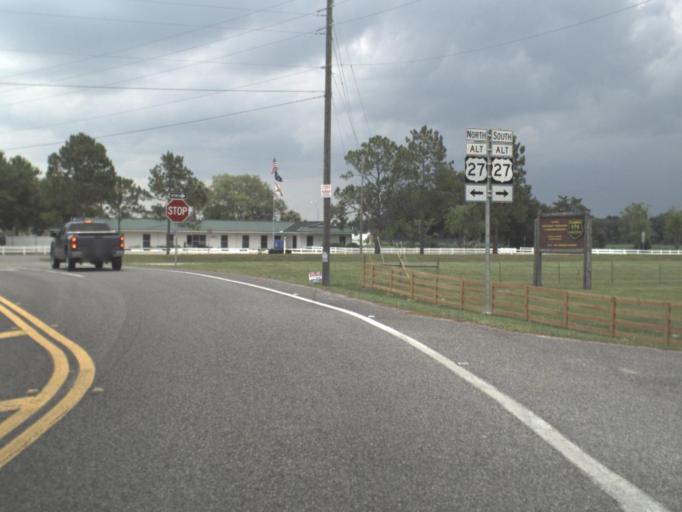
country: US
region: Florida
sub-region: Levy County
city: Chiefland
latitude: 29.4750
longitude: -82.8454
